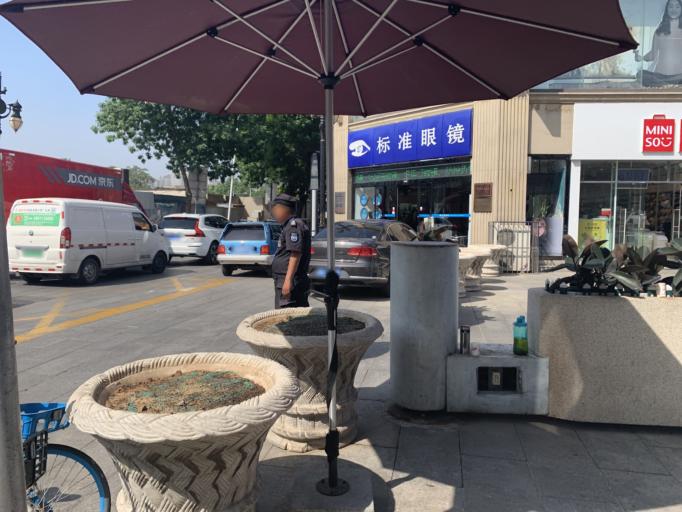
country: CN
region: Tianjin Shi
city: Nanshi
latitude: 39.1280
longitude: 117.1891
